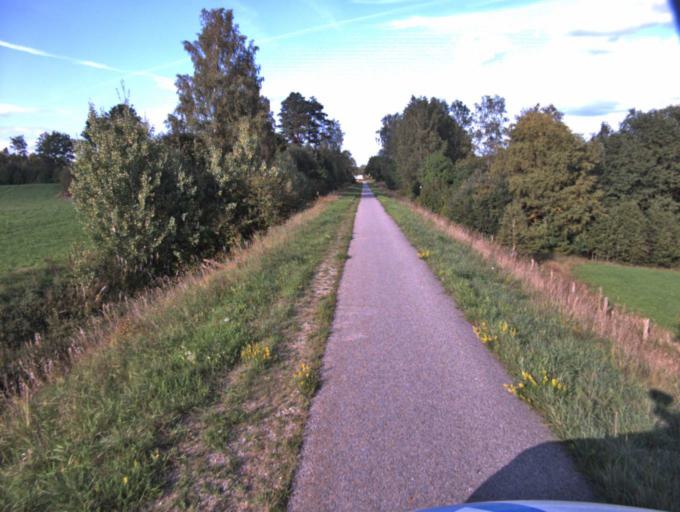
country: SE
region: Vaestra Goetaland
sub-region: Ulricehamns Kommun
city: Ulricehamn
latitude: 57.9176
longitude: 13.4850
